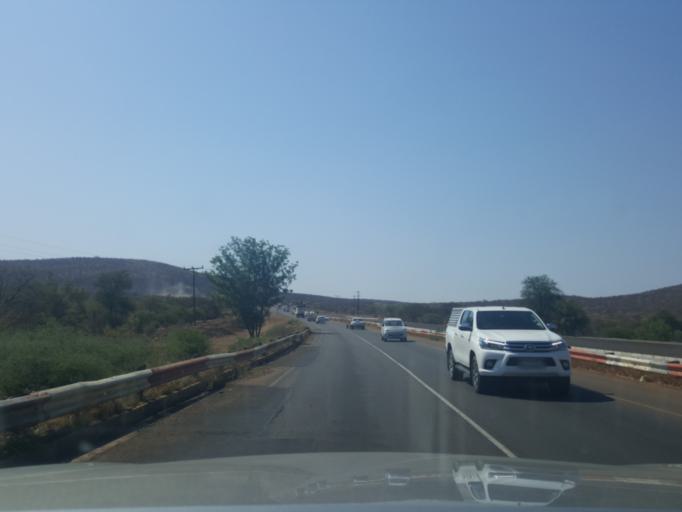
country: BW
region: Kweneng
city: Gabane
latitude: -24.7612
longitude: 25.8311
